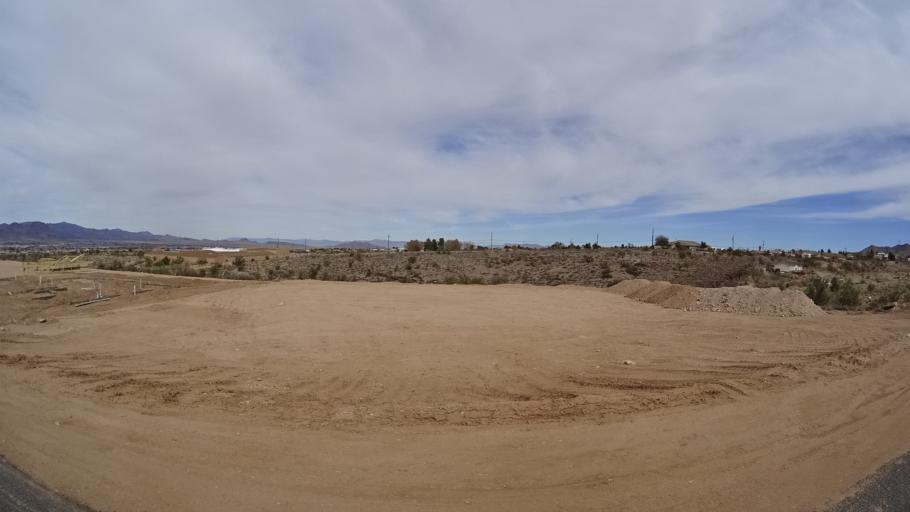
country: US
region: Arizona
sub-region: Mohave County
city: Kingman
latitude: 35.1773
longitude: -113.9959
